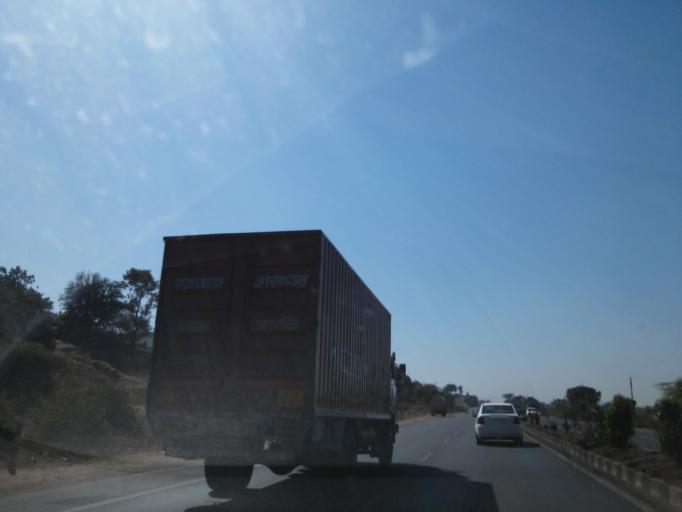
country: IN
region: Gujarat
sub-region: Sabar Kantha
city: Meghraj
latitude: 23.7524
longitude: 73.4393
